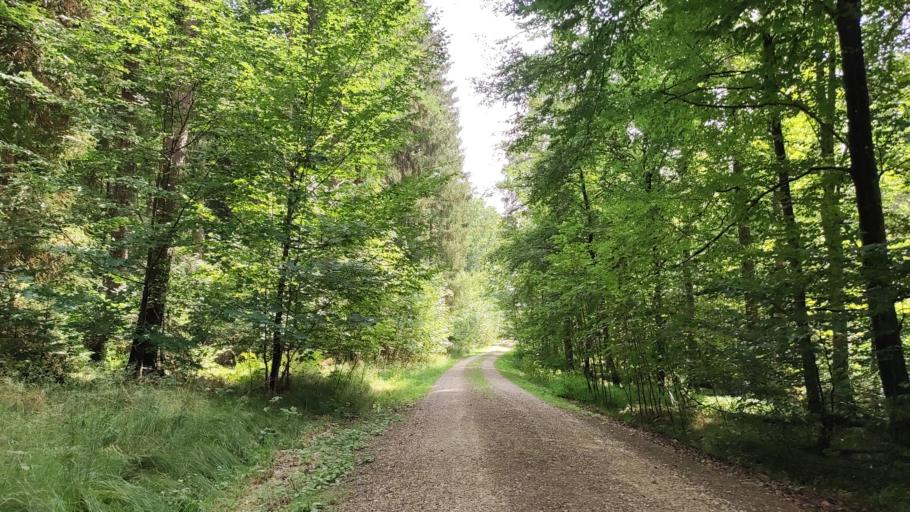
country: DE
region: Bavaria
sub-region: Swabia
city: Landensberg
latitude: 48.4262
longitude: 10.5172
